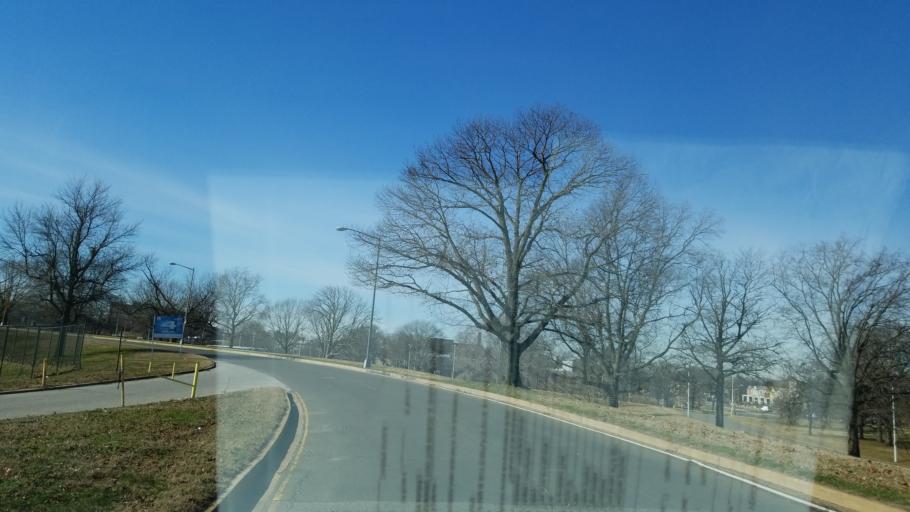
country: US
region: Maryland
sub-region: Prince George's County
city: Colmar Manor
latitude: 38.8920
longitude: -76.9723
